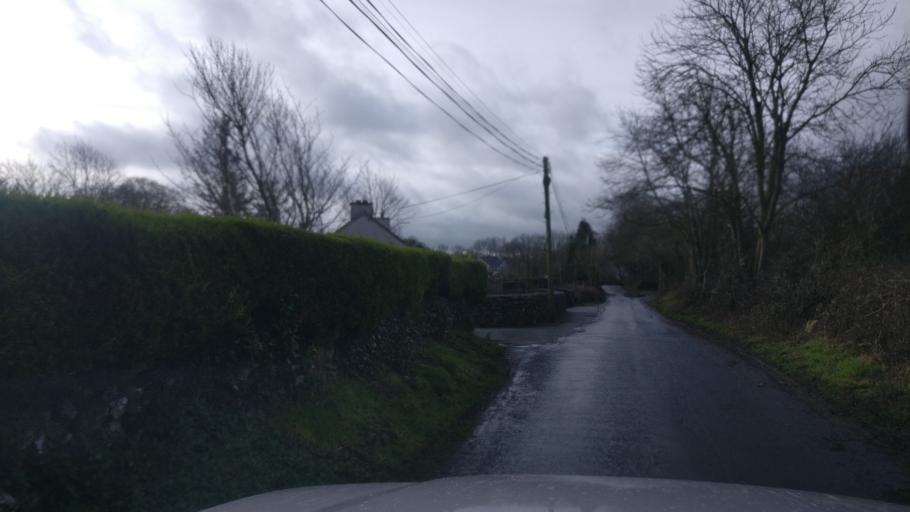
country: IE
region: Connaught
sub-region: County Galway
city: Athenry
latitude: 53.2745
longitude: -8.7682
